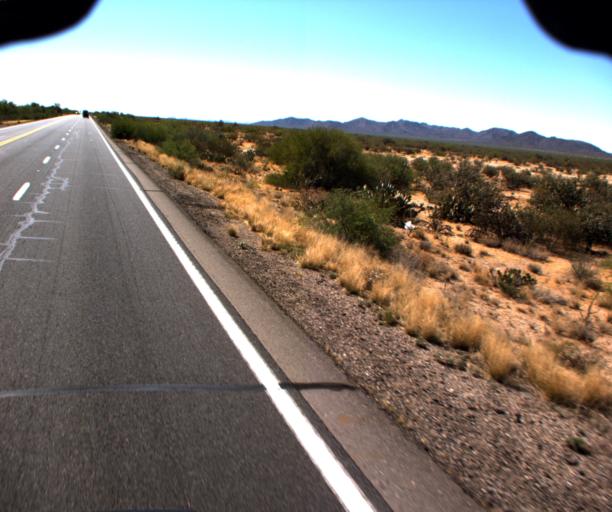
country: US
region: Arizona
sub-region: Yavapai County
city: Congress
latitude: 34.1532
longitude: -112.9935
